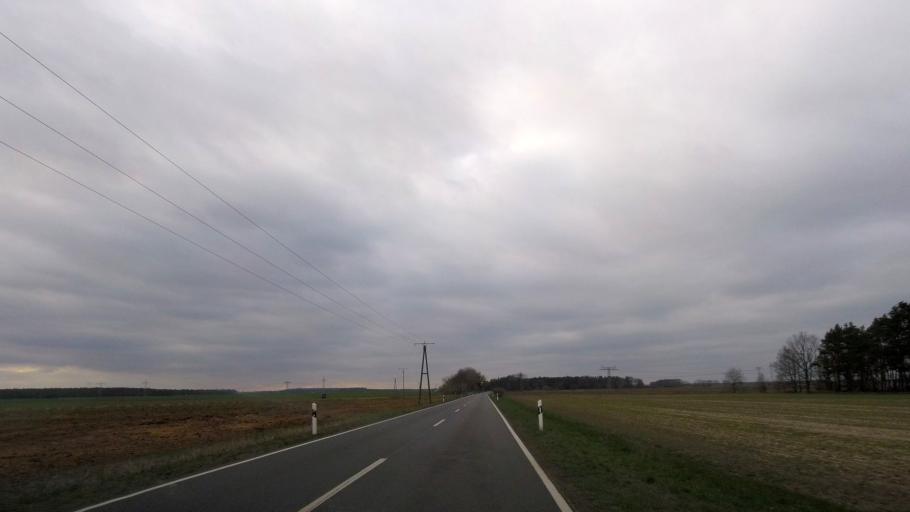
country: DE
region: Saxony-Anhalt
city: Kemberg
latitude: 51.7836
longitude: 12.6185
